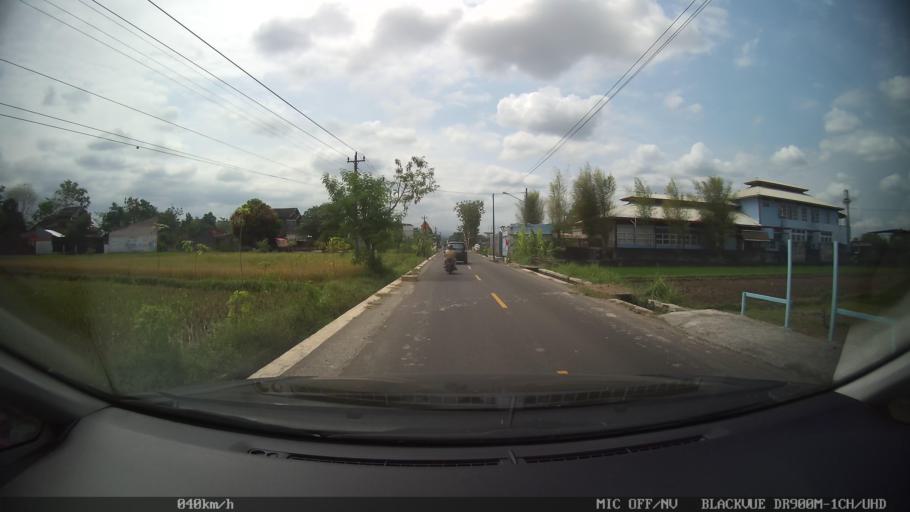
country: ID
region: Central Java
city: Candi Prambanan
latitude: -7.7423
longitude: 110.4815
